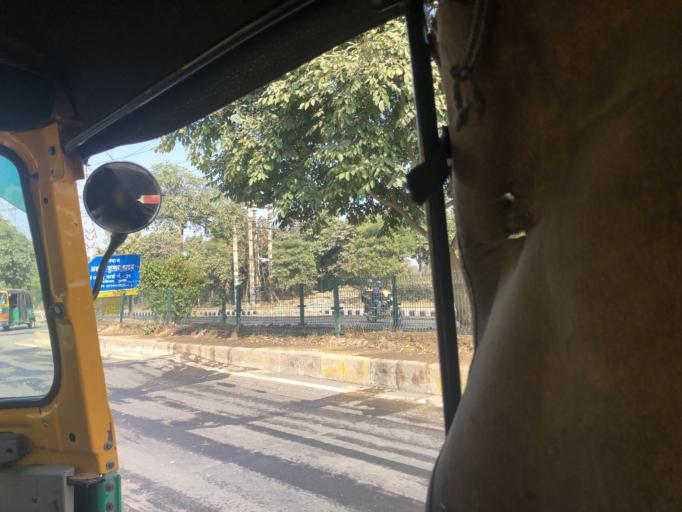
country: IN
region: Haryana
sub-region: Gurgaon
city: Gurgaon
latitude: 28.4436
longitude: 77.0836
